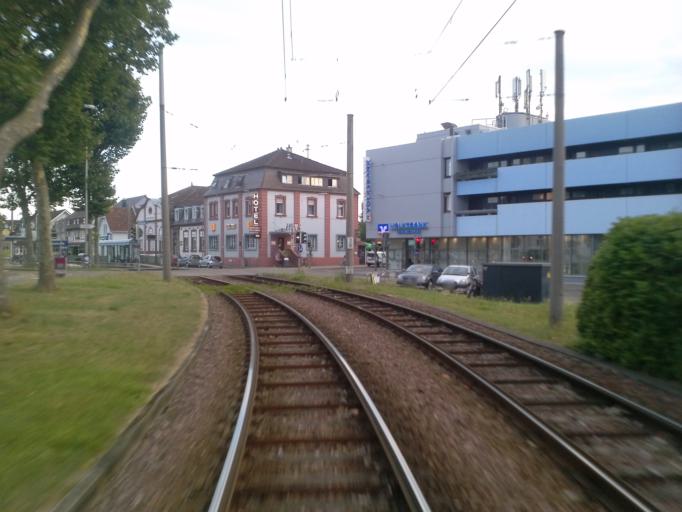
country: DE
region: Baden-Wuerttemberg
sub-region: Karlsruhe Region
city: Ettlingen
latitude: 48.9720
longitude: 8.4042
